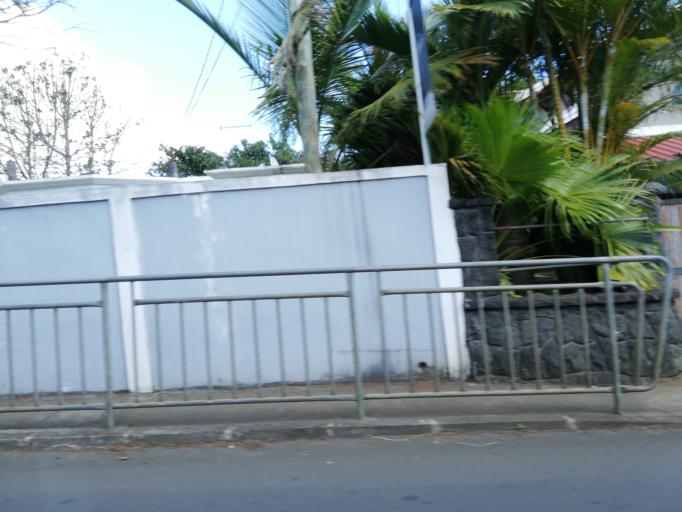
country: MU
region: Moka
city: Verdun
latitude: -20.2214
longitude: 57.5390
